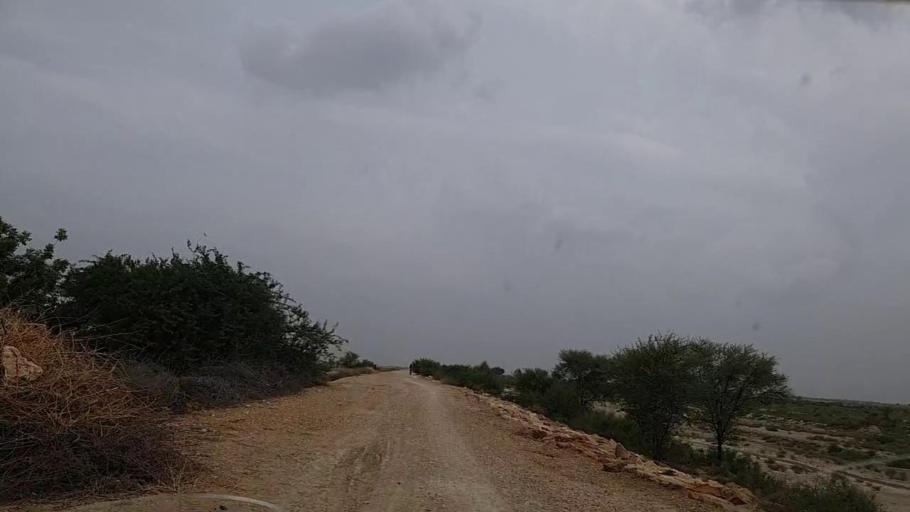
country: PK
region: Sindh
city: Johi
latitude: 26.7195
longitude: 67.5799
